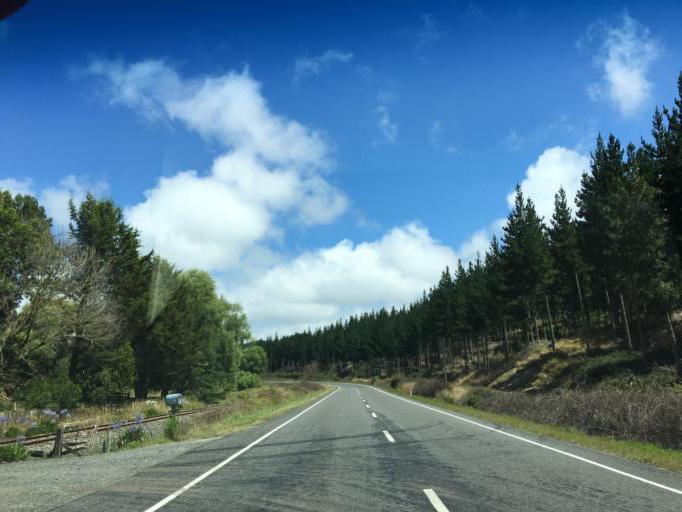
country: NZ
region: Hawke's Bay
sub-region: Wairoa District
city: Wairoa
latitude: -39.0350
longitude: 177.3115
